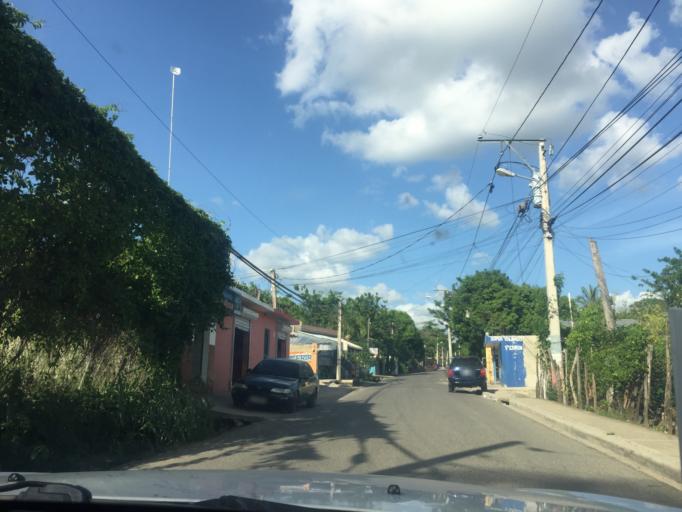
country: DO
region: Santiago
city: Tamboril
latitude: 19.4976
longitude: -70.6407
